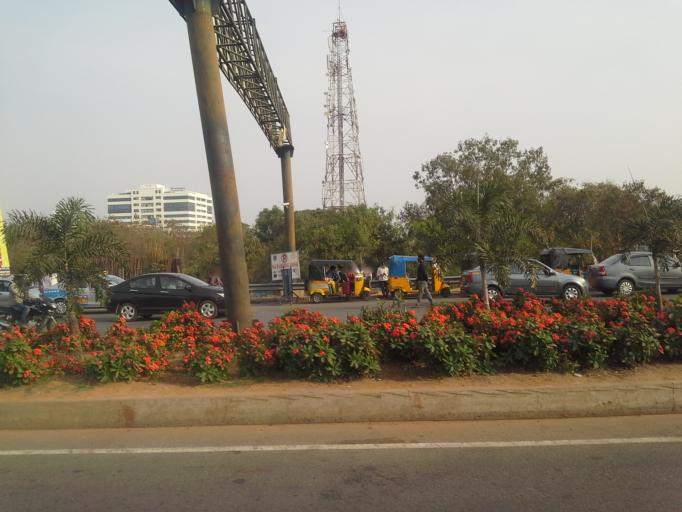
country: IN
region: Telangana
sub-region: Rangareddi
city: Kukatpalli
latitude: 17.4380
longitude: 78.3632
